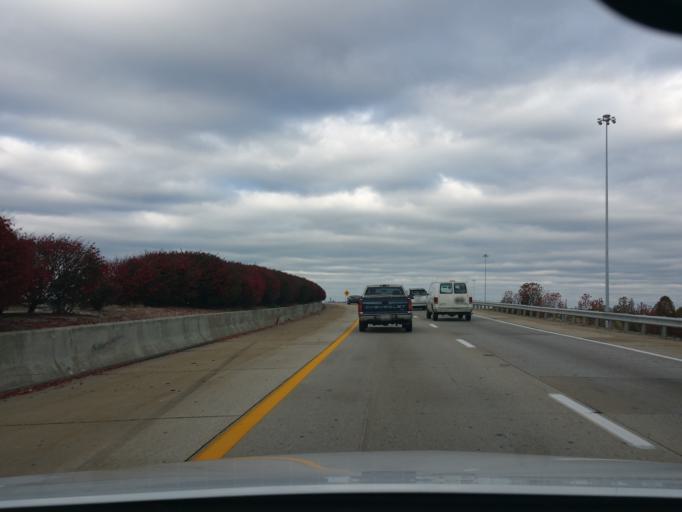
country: US
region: Kentucky
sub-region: Jefferson County
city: Saint Regis Park
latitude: 38.2368
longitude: -85.6194
